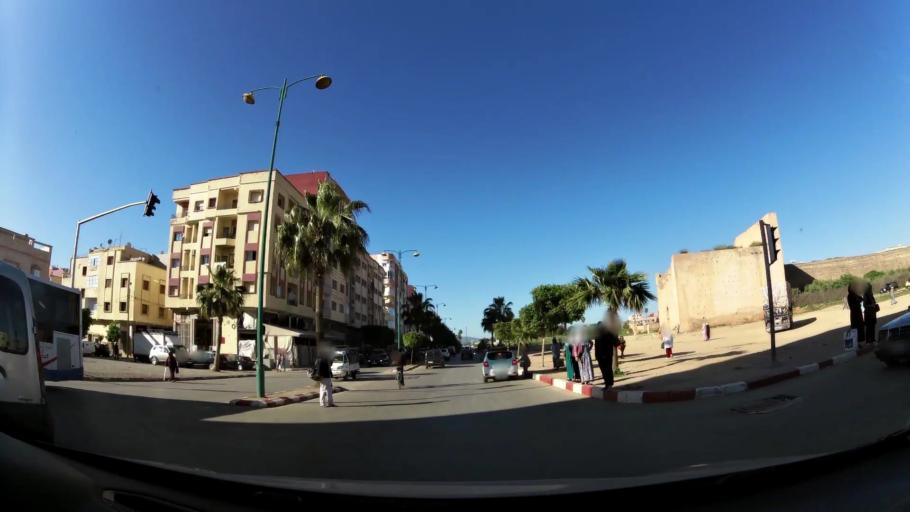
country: MA
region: Meknes-Tafilalet
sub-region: Meknes
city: Meknes
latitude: 33.8803
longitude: -5.5730
